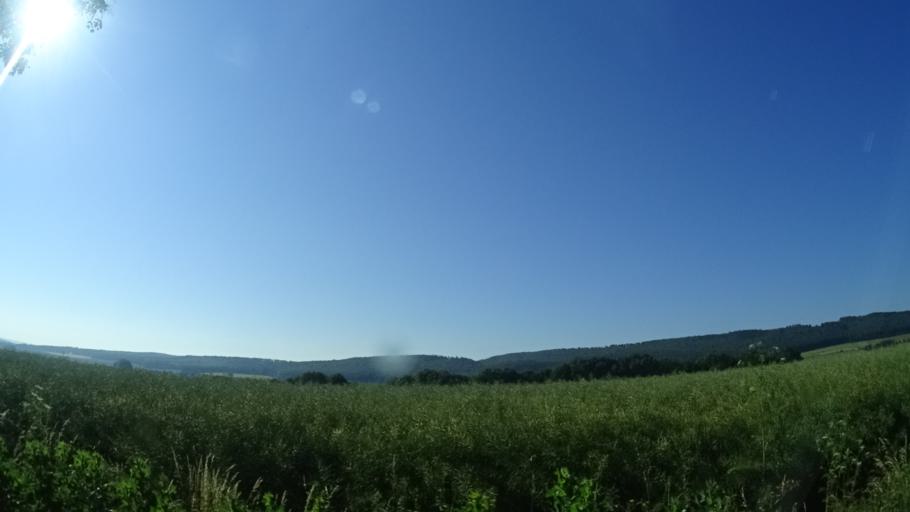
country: DE
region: Lower Saxony
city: Bad Salzdetfurth
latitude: 52.1028
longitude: 10.0734
